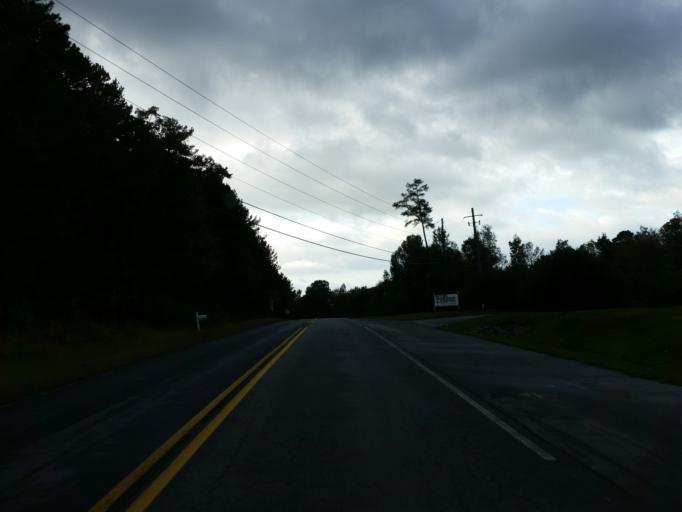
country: US
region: Georgia
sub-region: Bartow County
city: Emerson
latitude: 34.1154
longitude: -84.7946
